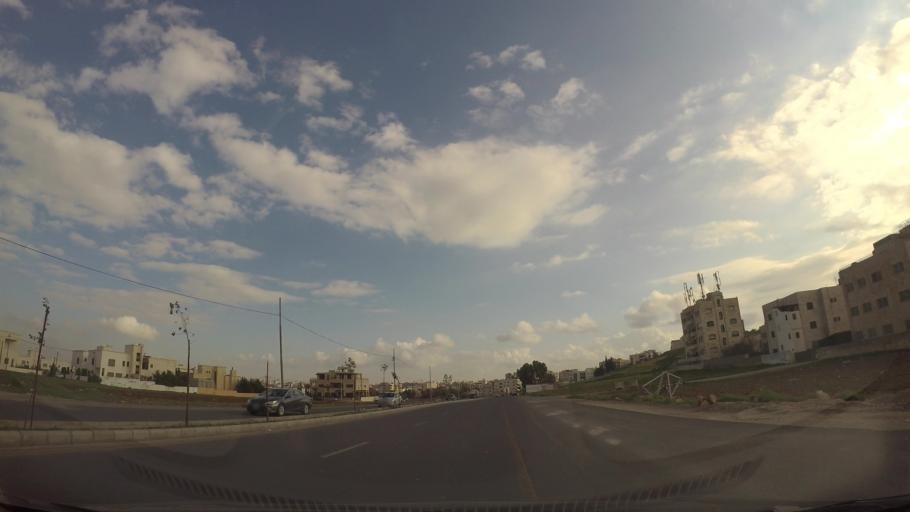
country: JO
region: Amman
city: Umm as Summaq
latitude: 31.9147
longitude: 35.8499
